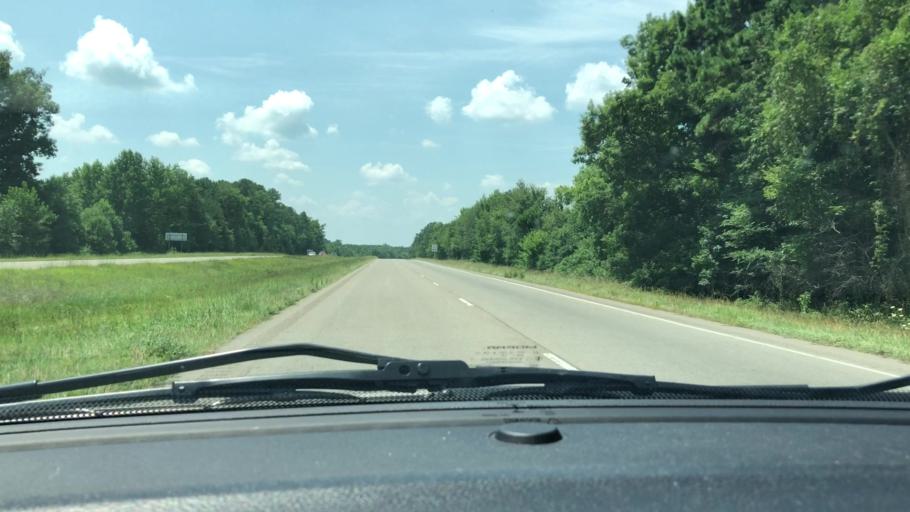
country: US
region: North Carolina
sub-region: Chatham County
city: Farmville
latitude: 35.6075
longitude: -79.3326
